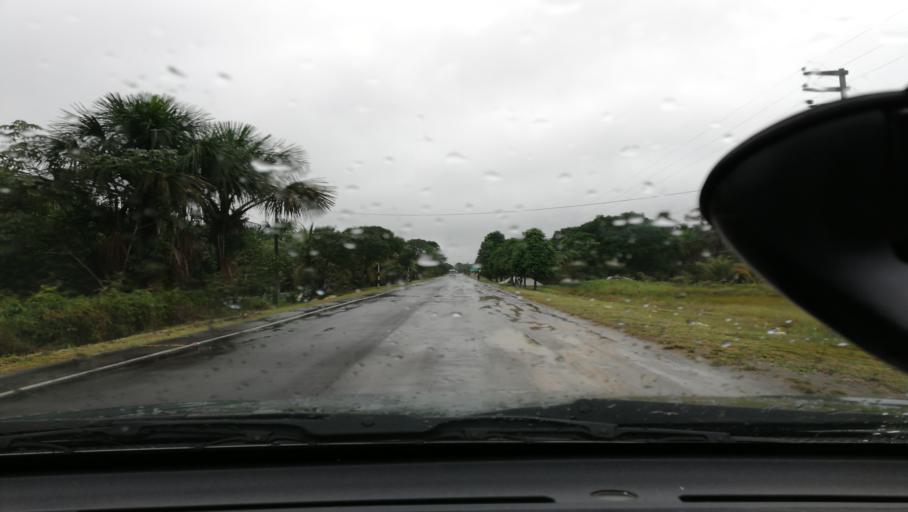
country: PE
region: Loreto
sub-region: Provincia de Maynas
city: San Juan
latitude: -4.1023
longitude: -73.4556
